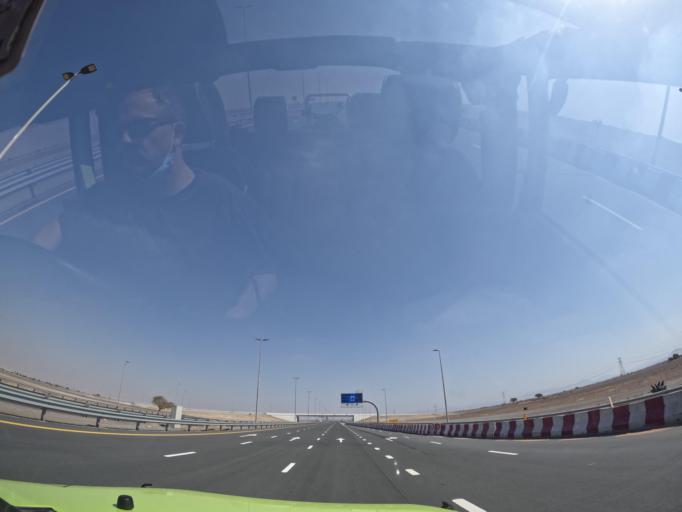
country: AE
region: Ash Shariqah
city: Adh Dhayd
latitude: 24.9284
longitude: 55.8125
